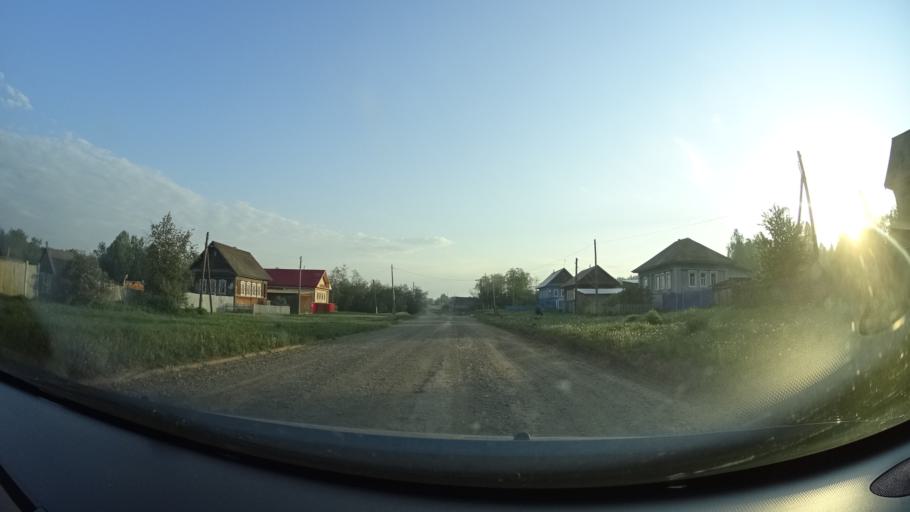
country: RU
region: Perm
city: Kuyeda
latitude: 56.6591
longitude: 55.6927
